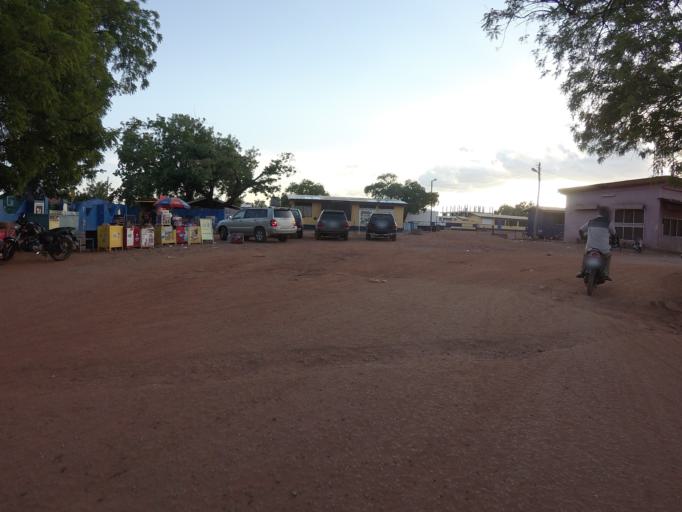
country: GH
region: Upper East
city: Navrongo
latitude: 10.9953
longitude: -1.1133
